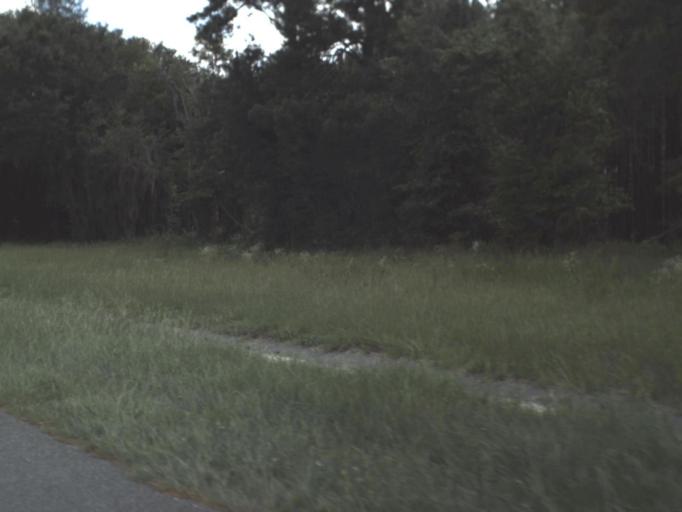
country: US
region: Florida
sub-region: Columbia County
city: Watertown
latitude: 30.0149
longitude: -82.5975
